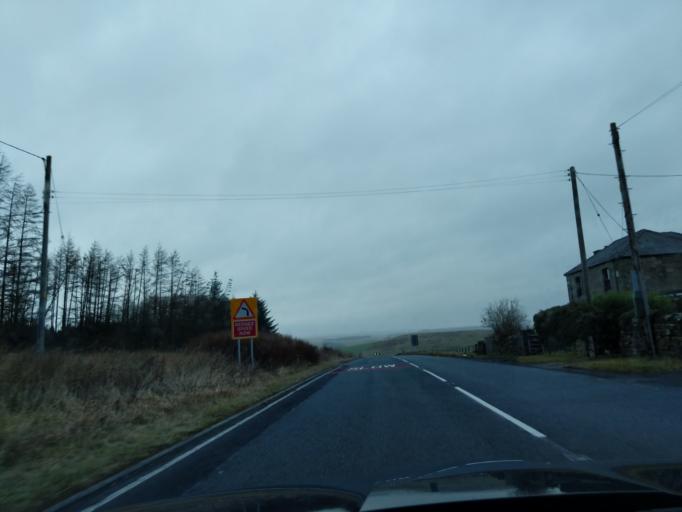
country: GB
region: England
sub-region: Northumberland
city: Otterburn
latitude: 55.2097
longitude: -2.1051
